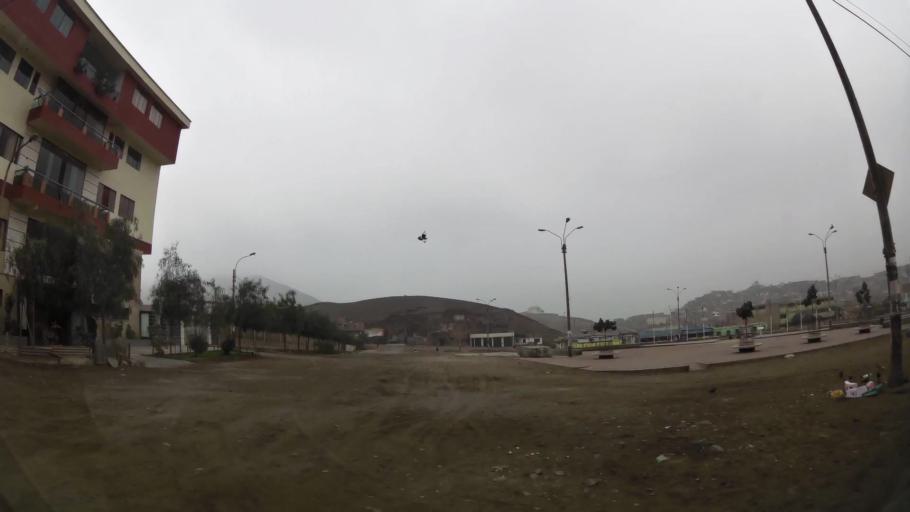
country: PE
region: Lima
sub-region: Lima
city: Santa Rosa
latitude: -11.8150
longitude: -77.1371
